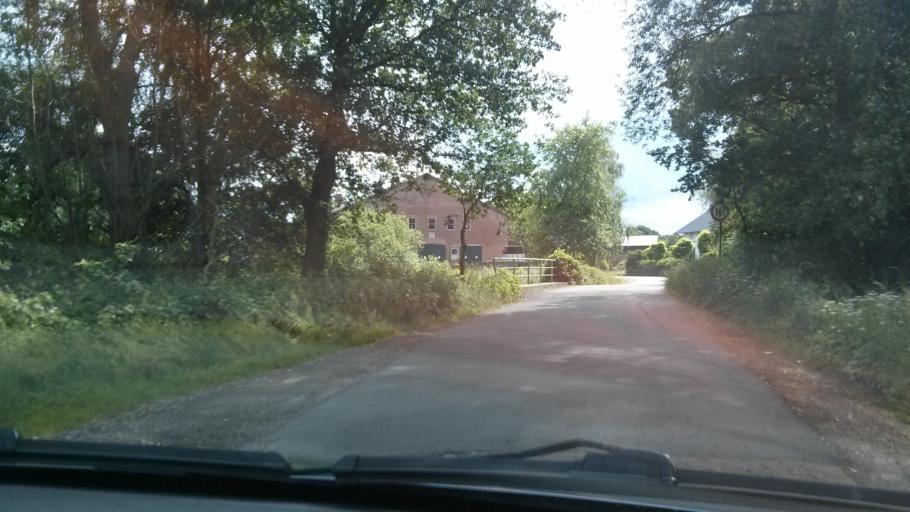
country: DE
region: Lower Saxony
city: Schiffdorf
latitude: 53.5102
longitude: 8.6965
